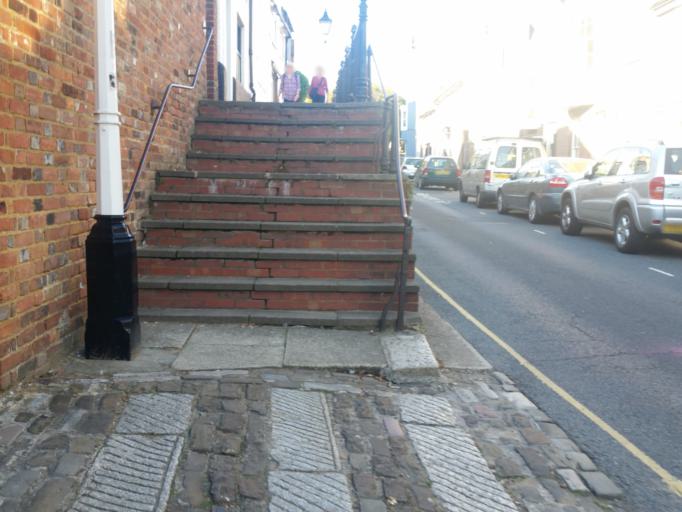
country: GB
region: England
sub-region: East Sussex
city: Hastings
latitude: 50.8590
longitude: 0.5932
